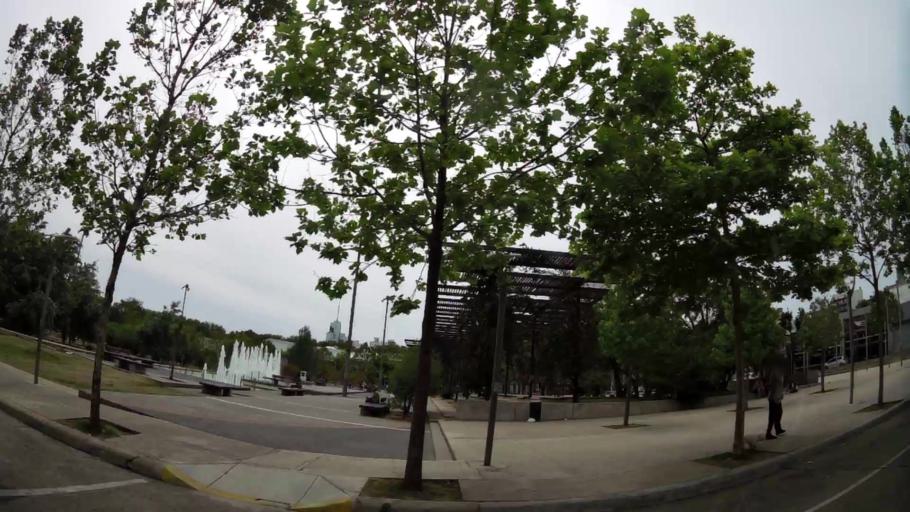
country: UY
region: Montevideo
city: Montevideo
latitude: -34.8974
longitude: -56.1726
